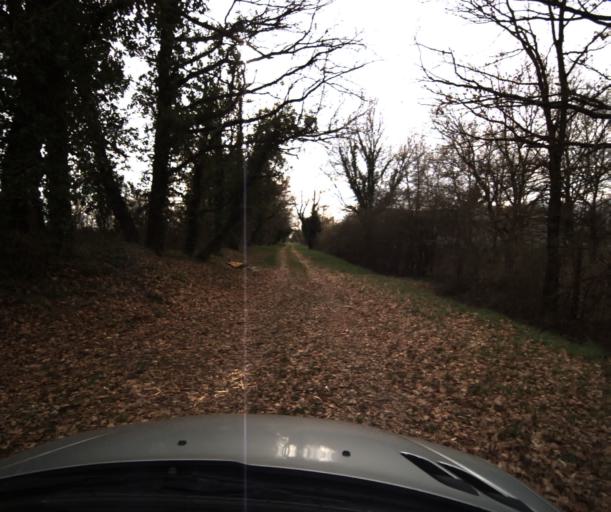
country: FR
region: Midi-Pyrenees
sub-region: Departement du Tarn-et-Garonne
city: Montauban
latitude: 44.0307
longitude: 1.4049
